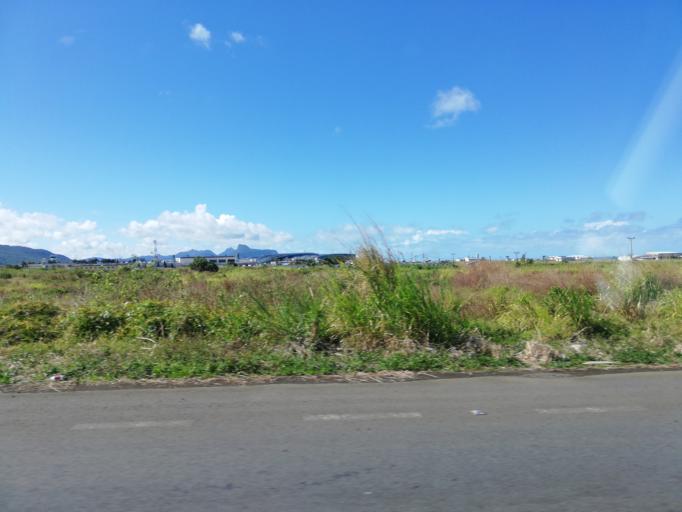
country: MU
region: Grand Port
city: Plaine Magnien
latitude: -20.4407
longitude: 57.6732
